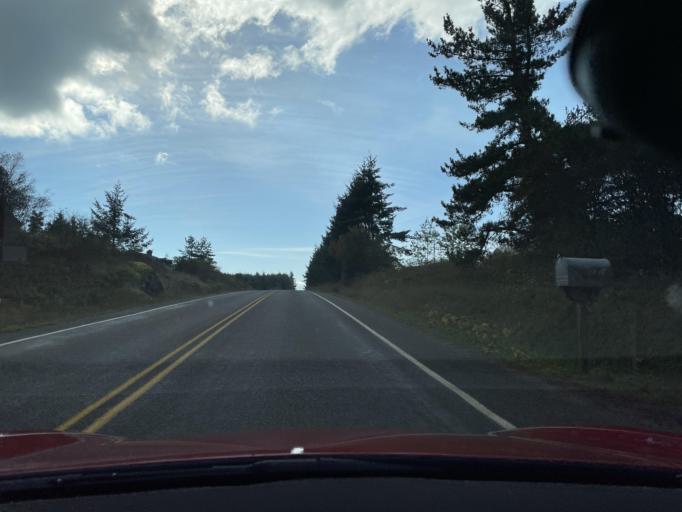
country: US
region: Washington
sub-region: San Juan County
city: Friday Harbor
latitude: 48.4844
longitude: -123.0316
